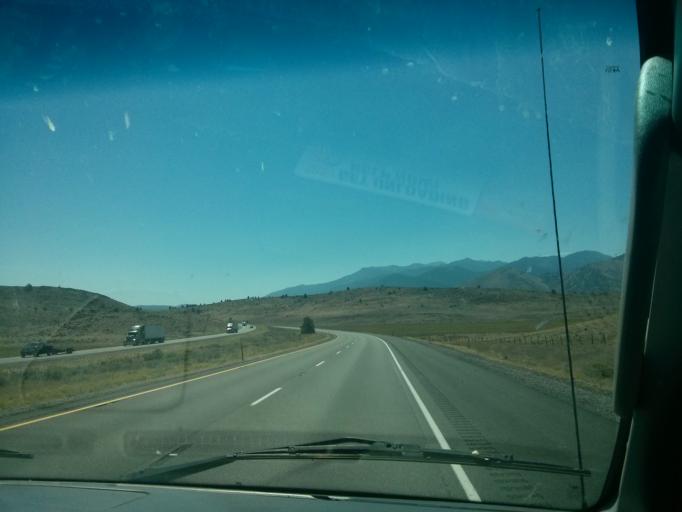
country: US
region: California
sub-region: Siskiyou County
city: Weed
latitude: 41.5101
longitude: -122.4731
